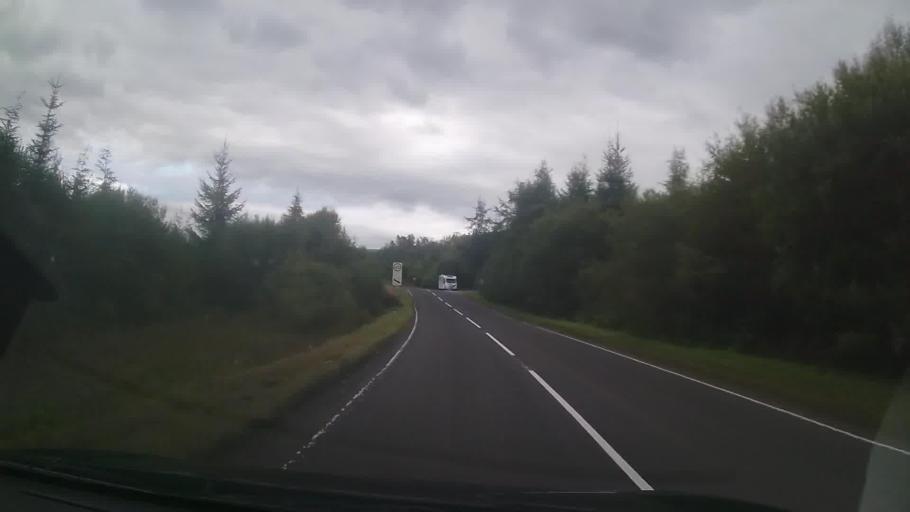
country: GB
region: Scotland
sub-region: Argyll and Bute
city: Garelochhead
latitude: 56.2425
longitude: -5.0894
